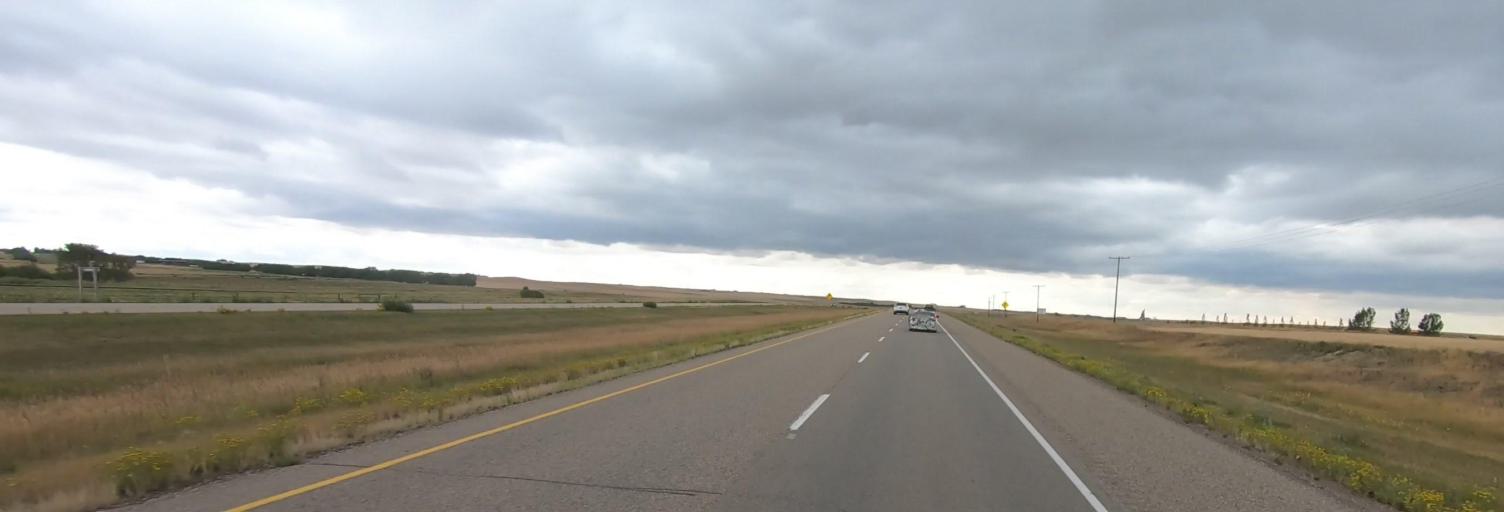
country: CA
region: Saskatchewan
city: Swift Current
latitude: 50.1616
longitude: -108.2783
